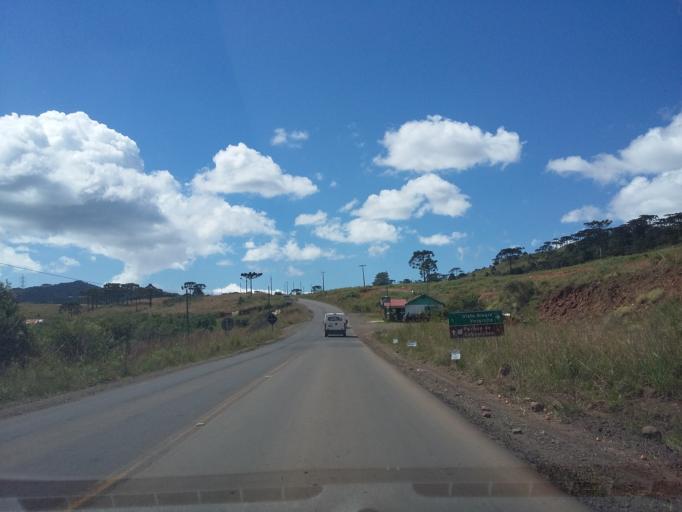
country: BR
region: Santa Catarina
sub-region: Lauro Muller
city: Lauro Muller
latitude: -28.3392
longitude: -49.6444
